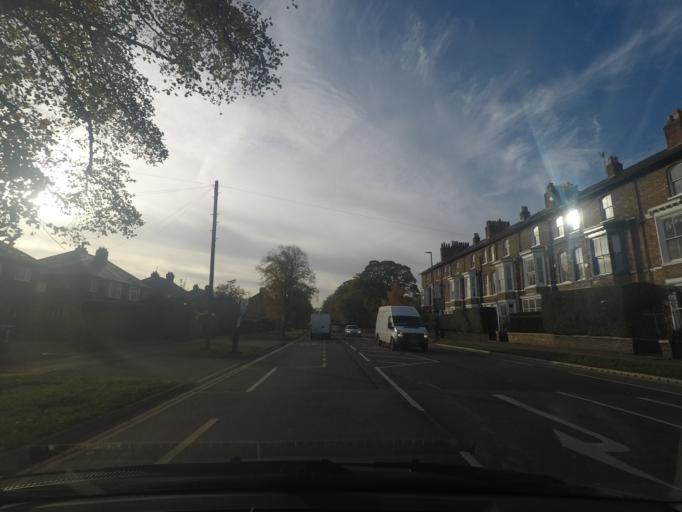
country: GB
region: England
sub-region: City of York
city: Fulford
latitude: 53.9404
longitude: -1.0741
